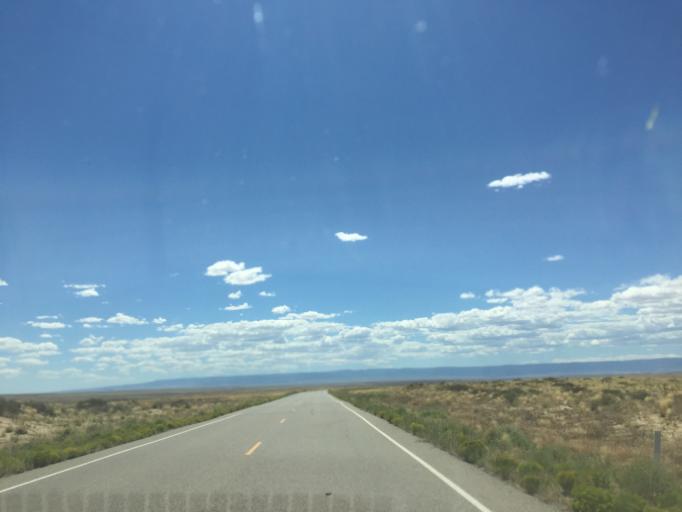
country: US
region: New Mexico
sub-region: San Juan County
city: Upper Fruitland
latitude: 36.4105
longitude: -108.4477
